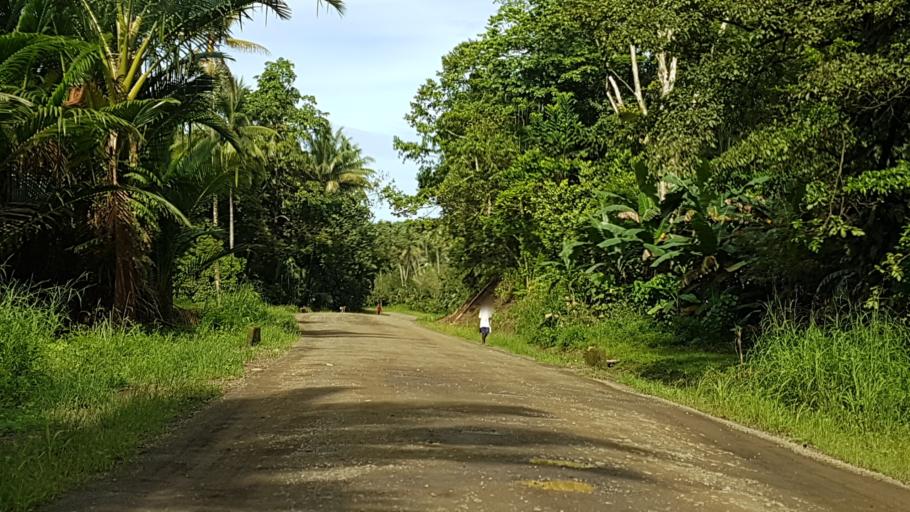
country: PG
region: Milne Bay
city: Alotau
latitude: -10.3419
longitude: 150.5992
